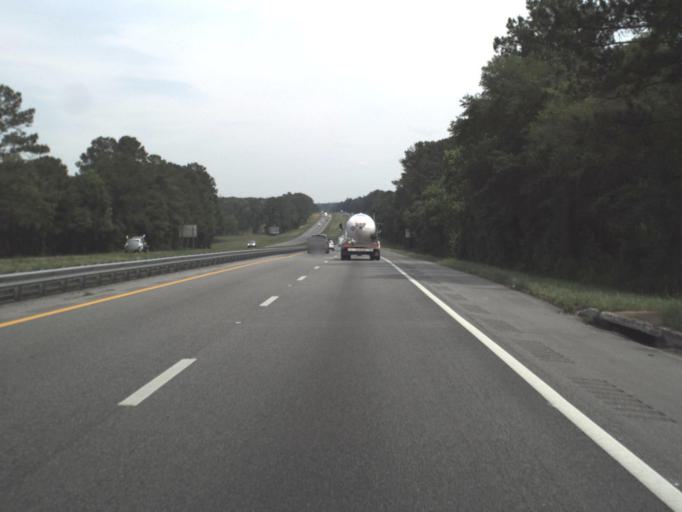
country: US
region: Florida
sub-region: Suwannee County
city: Live Oak
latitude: 30.3258
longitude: -82.9562
